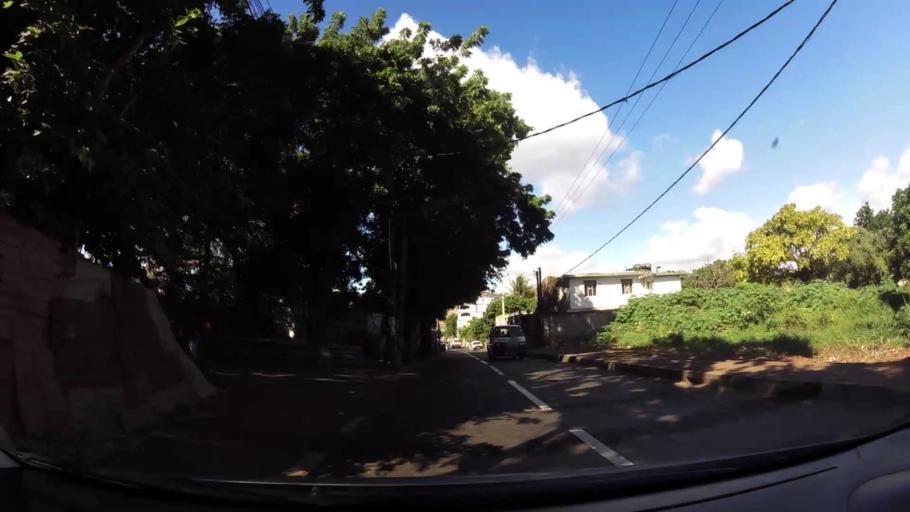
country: MU
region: Pamplemousses
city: Le Hochet
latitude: -20.1375
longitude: 57.5230
